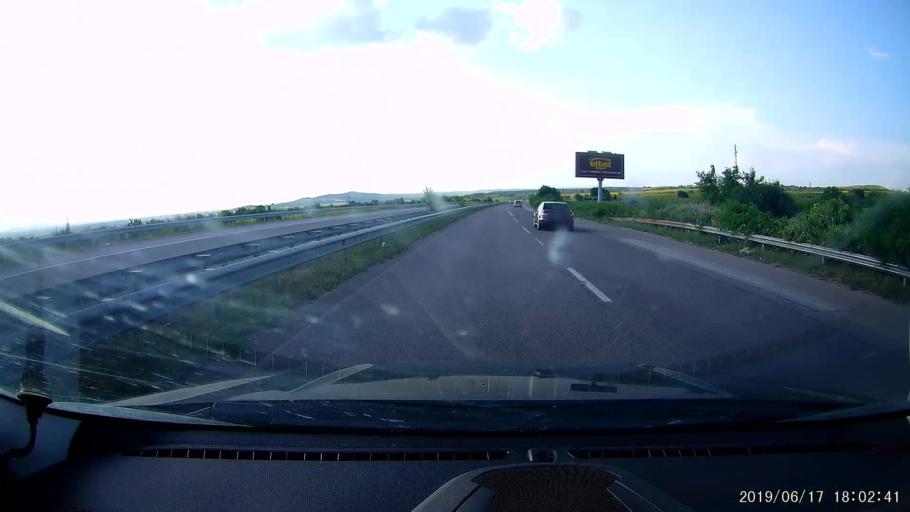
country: BG
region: Khaskovo
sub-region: Obshtina Svilengrad
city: Svilengrad
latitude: 41.7639
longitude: 26.2276
